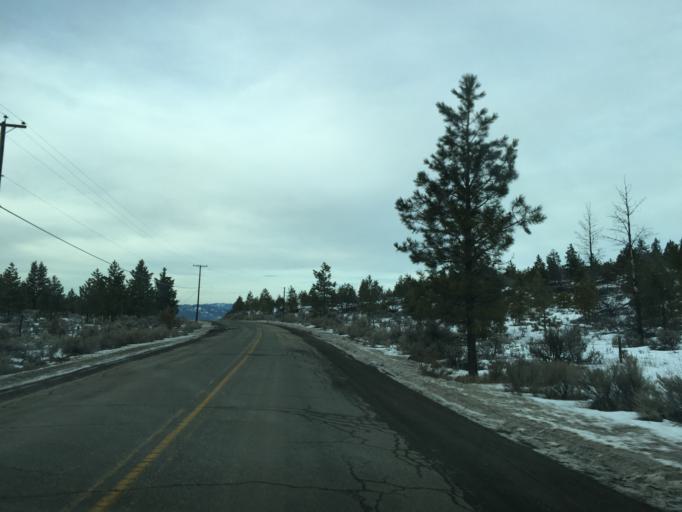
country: CA
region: British Columbia
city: Kamloops
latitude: 50.6466
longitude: -120.4511
